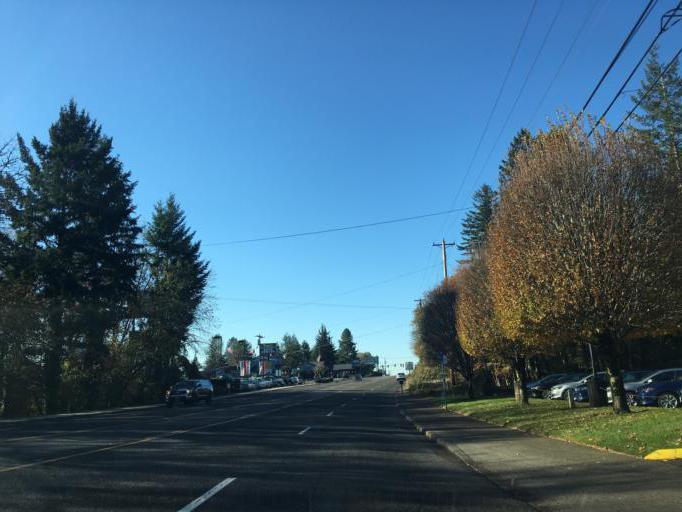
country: US
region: Oregon
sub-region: Washington County
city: West Slope
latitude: 45.4942
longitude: -122.7753
